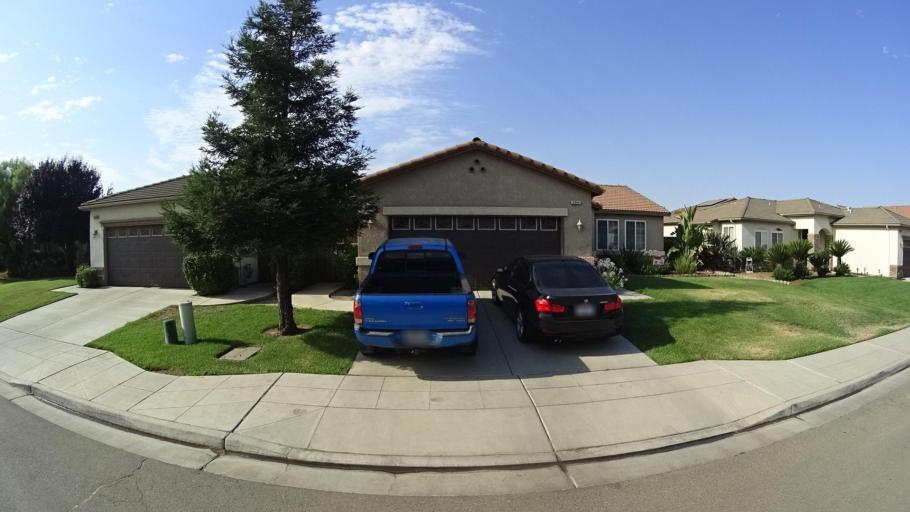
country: US
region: California
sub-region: Fresno County
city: Sunnyside
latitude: 36.7211
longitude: -119.7021
